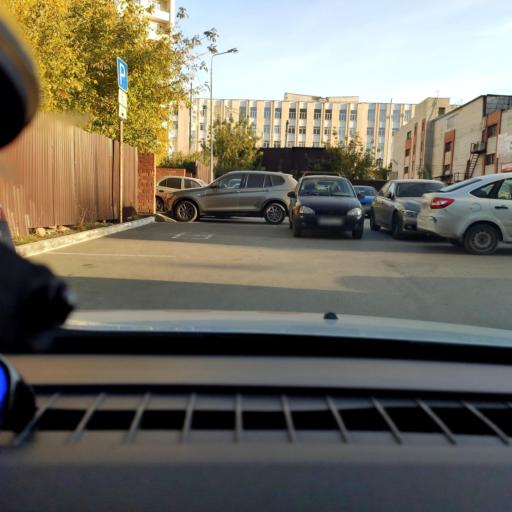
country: RU
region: Samara
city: Samara
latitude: 53.2162
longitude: 50.1717
